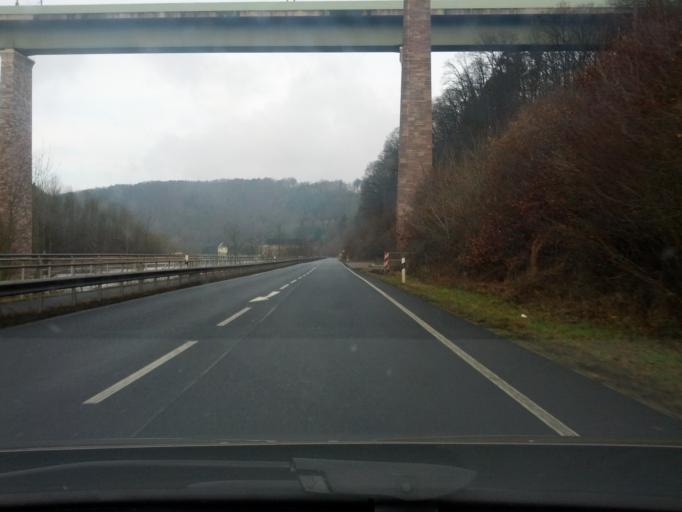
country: DE
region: Lower Saxony
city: Scheden
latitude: 51.4042
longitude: 9.7158
